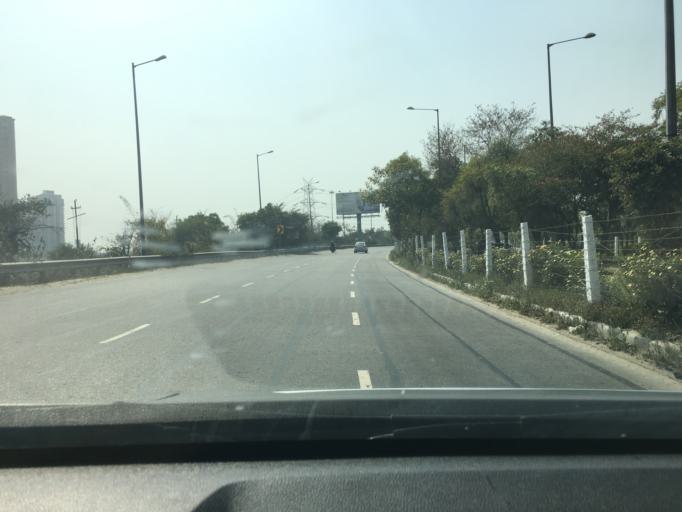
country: IN
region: Uttar Pradesh
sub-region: Gautam Buddha Nagar
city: Greater Noida
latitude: 28.4454
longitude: 77.4863
